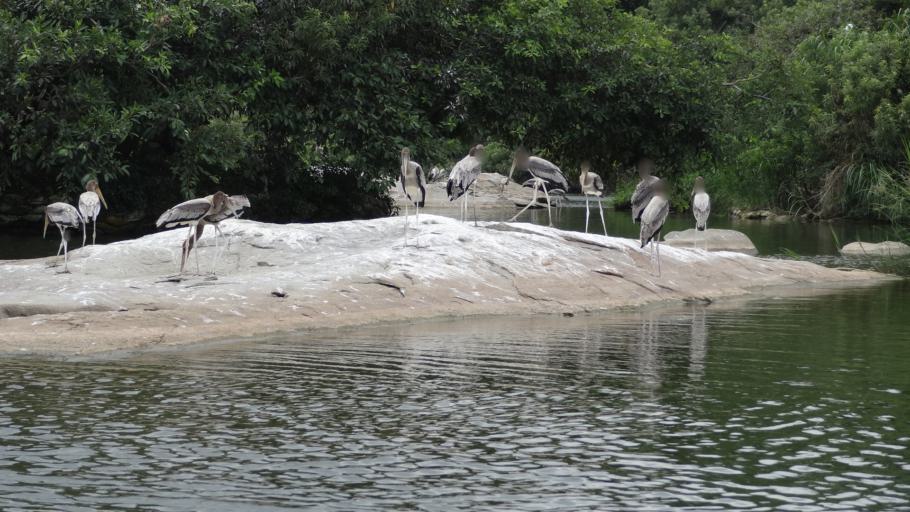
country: IN
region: Karnataka
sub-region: Mandya
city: Shrirangapattana
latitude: 12.4239
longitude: 76.6535
